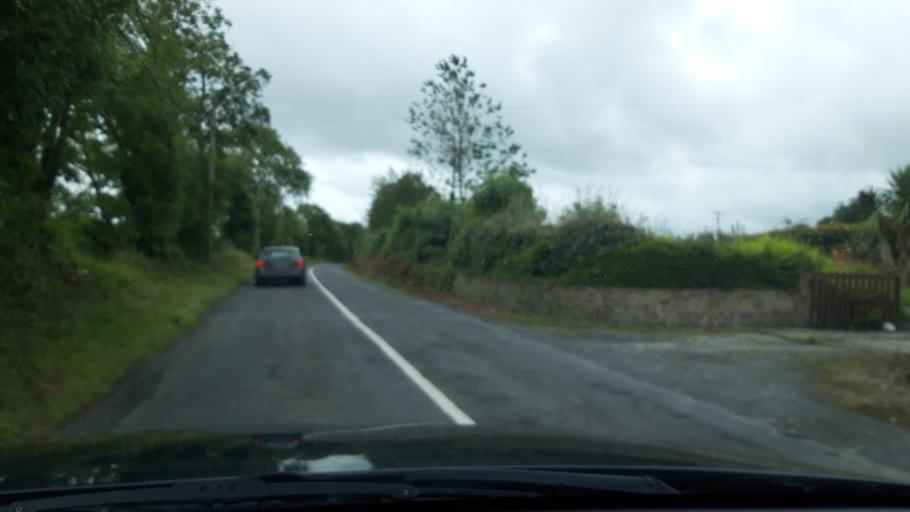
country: IE
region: Munster
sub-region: County Cork
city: Youghal
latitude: 52.1599
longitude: -7.8451
